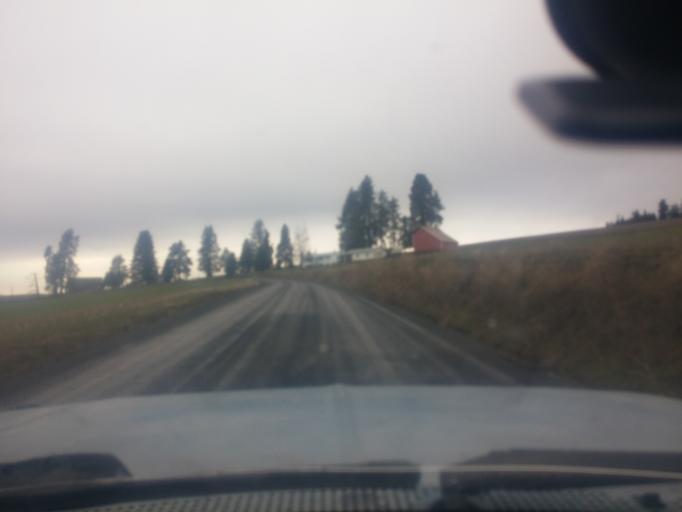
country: US
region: Idaho
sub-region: Latah County
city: Moscow
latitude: 46.9160
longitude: -116.8507
